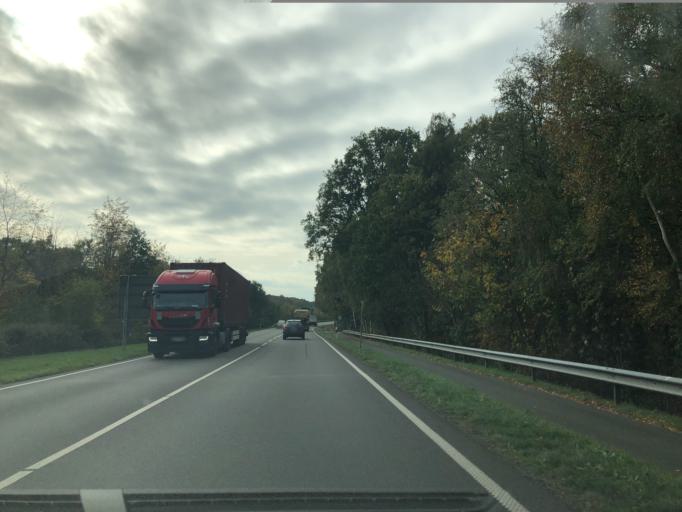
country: DE
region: Lower Saxony
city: Friesoythe
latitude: 53.0559
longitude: 7.8019
